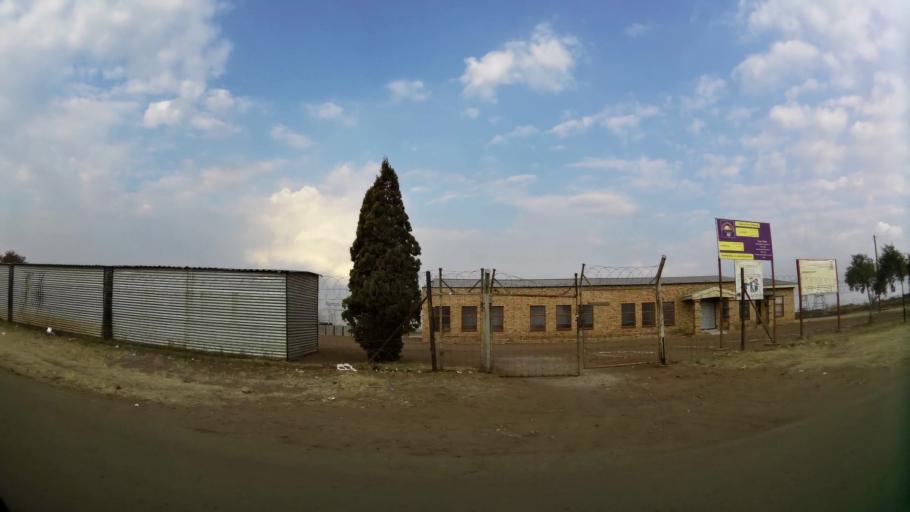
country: ZA
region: Gauteng
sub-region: Sedibeng District Municipality
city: Vanderbijlpark
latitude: -26.6948
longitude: 27.8777
